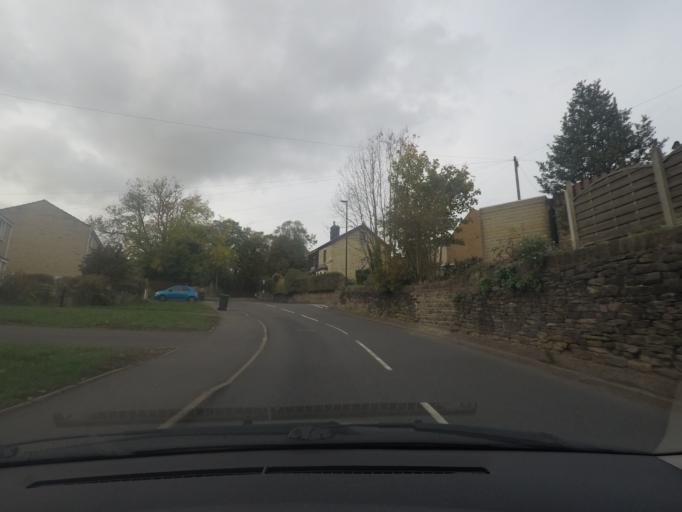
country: GB
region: England
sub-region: Sheffield
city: Oughtibridge
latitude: 53.4228
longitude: -1.4988
